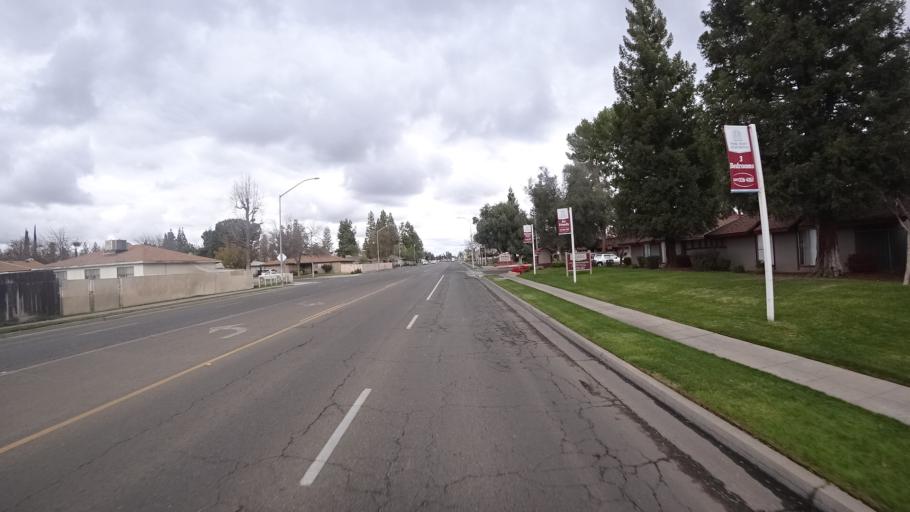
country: US
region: California
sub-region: Fresno County
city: Fresno
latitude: 36.8053
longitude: -119.8444
